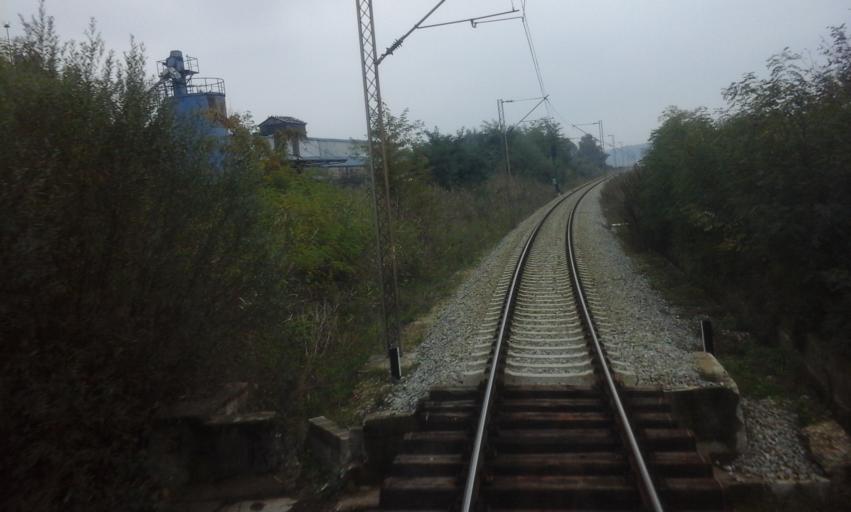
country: RS
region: Central Serbia
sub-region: Belgrade
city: Mladenovac
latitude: 44.4755
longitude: 20.6637
